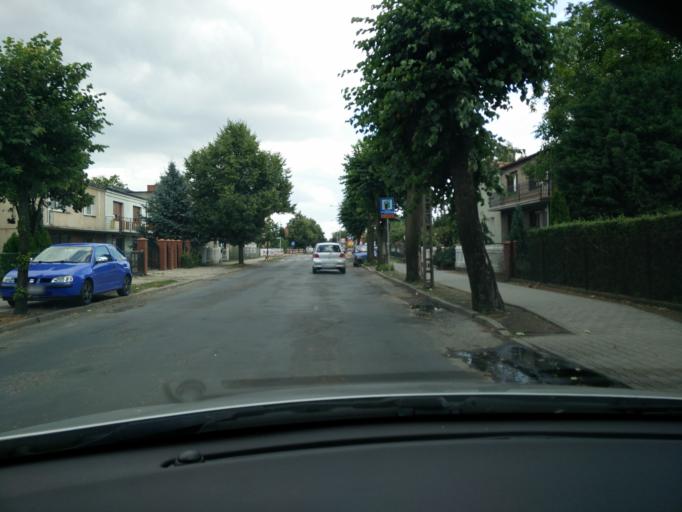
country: PL
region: Greater Poland Voivodeship
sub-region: Powiat sredzki
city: Sroda Wielkopolska
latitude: 52.2289
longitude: 17.2656
